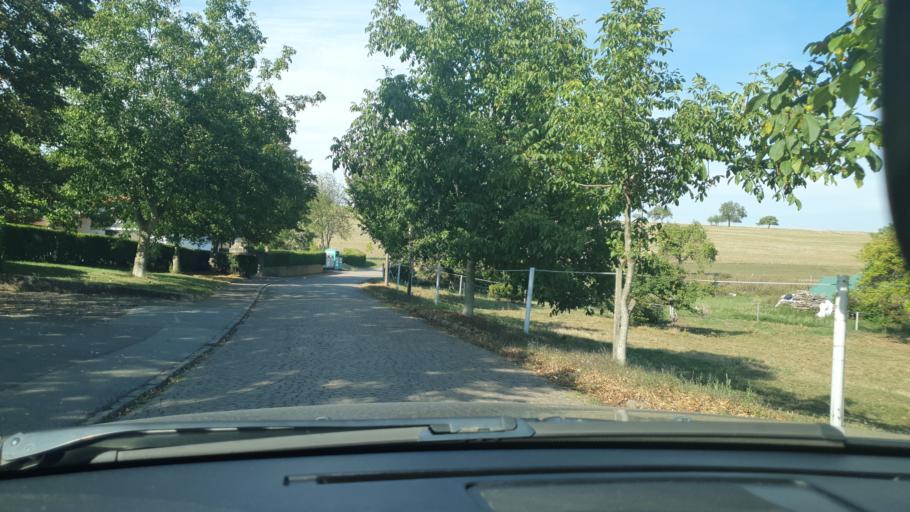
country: DE
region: Rheinland-Pfalz
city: Kashofen
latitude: 49.3273
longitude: 7.4211
